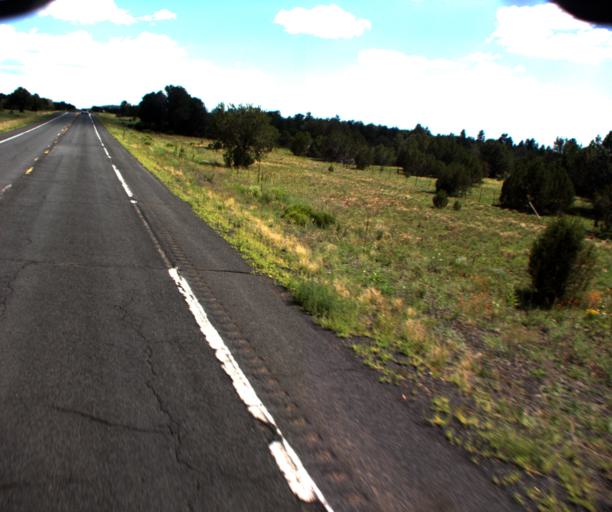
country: US
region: Arizona
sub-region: Coconino County
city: Williams
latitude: 35.3572
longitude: -112.1672
